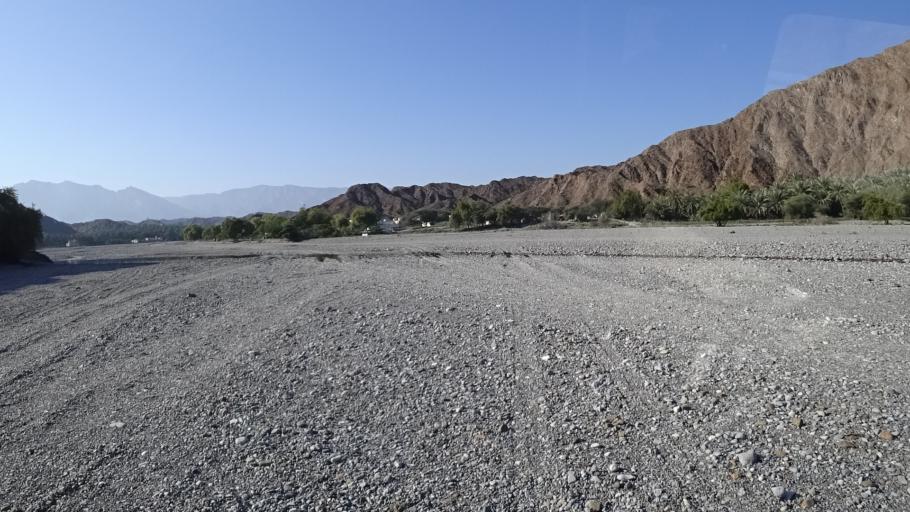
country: OM
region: Al Batinah
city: Bayt al `Awabi
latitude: 23.3969
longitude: 57.6633
